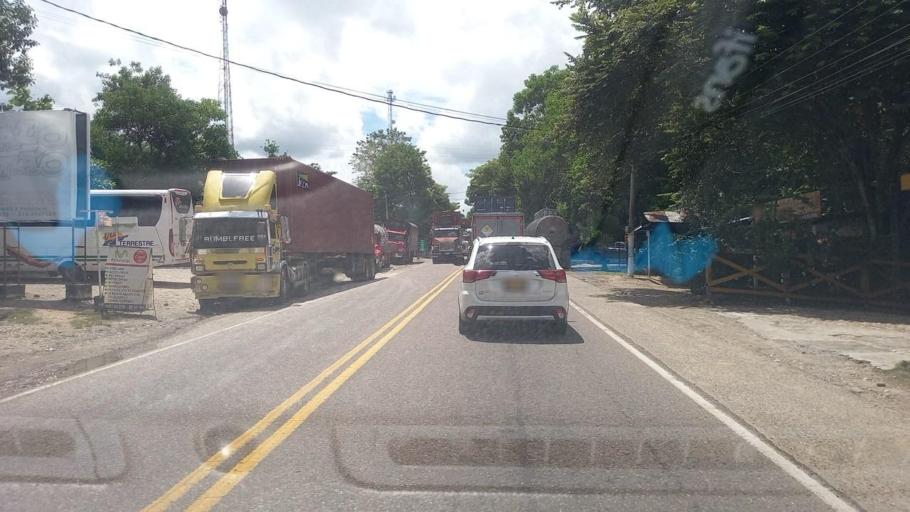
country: CO
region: Santander
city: Puerto Parra
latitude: 6.6464
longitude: -73.9515
